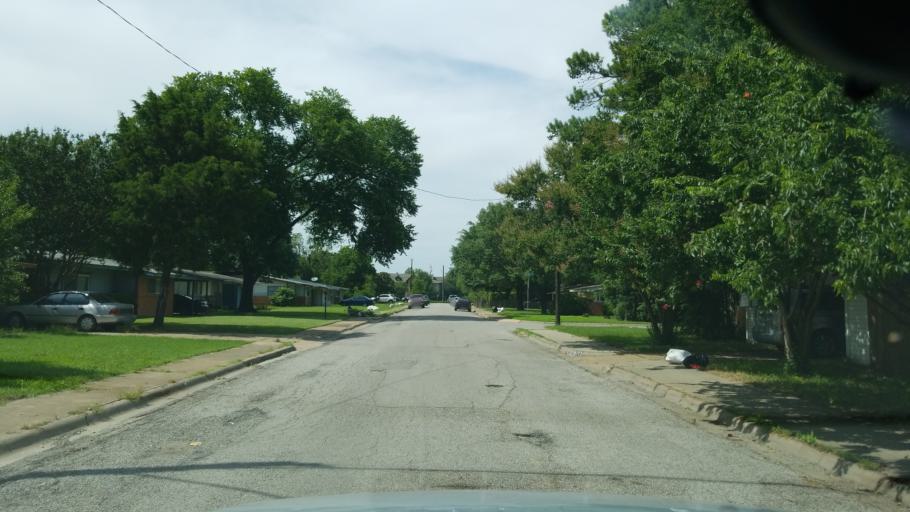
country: US
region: Texas
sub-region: Dallas County
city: Irving
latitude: 32.8317
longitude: -96.9480
